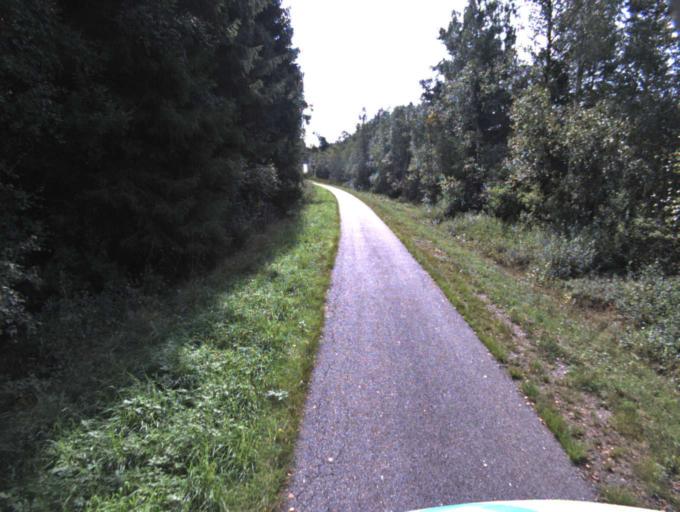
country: SE
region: Vaestra Goetaland
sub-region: Tranemo Kommun
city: Limmared
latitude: 57.6146
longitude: 13.3434
